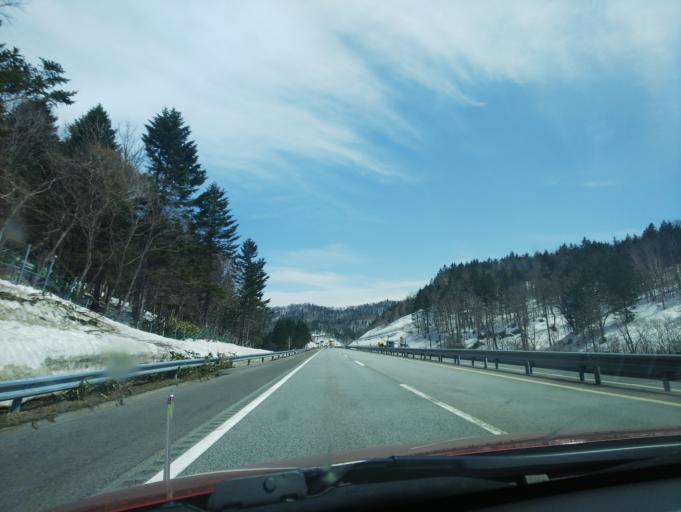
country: JP
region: Hokkaido
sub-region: Asahikawa-shi
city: Asahikawa
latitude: 43.7808
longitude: 142.2023
